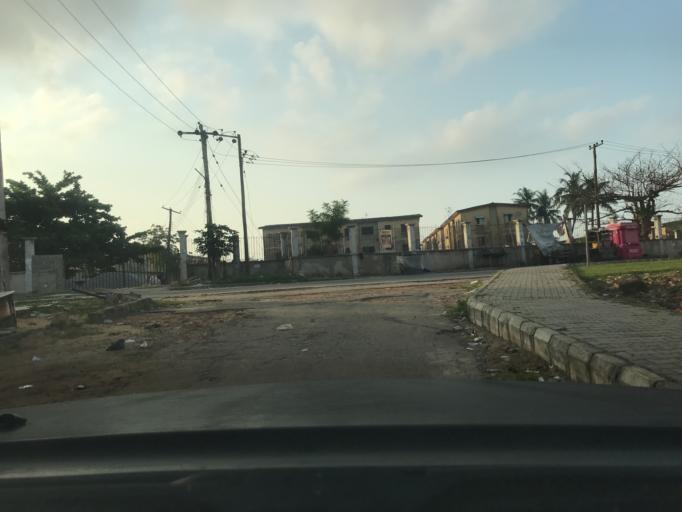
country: NG
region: Lagos
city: Festac Town
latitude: 6.4646
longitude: 3.3050
